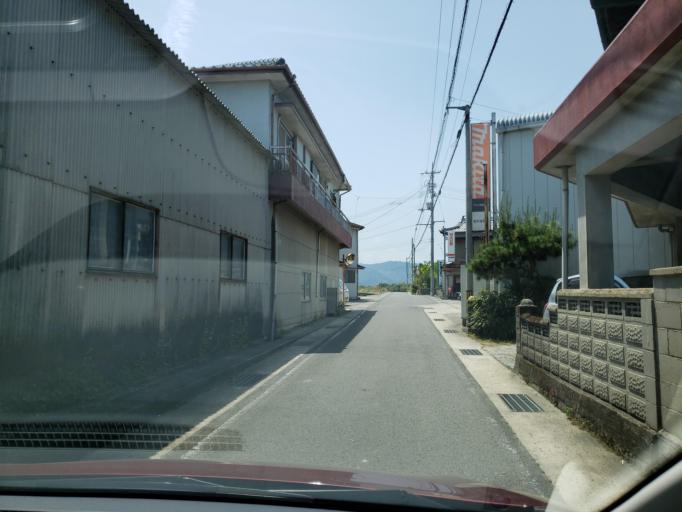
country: JP
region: Tokushima
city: Wakimachi
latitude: 34.0877
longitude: 134.2170
